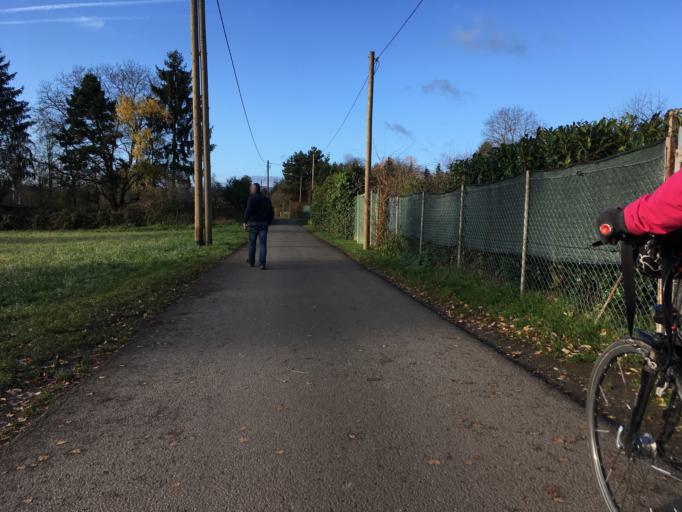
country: DE
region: Hesse
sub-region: Regierungsbezirk Darmstadt
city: Wiesbaden
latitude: 50.0593
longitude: 8.2282
